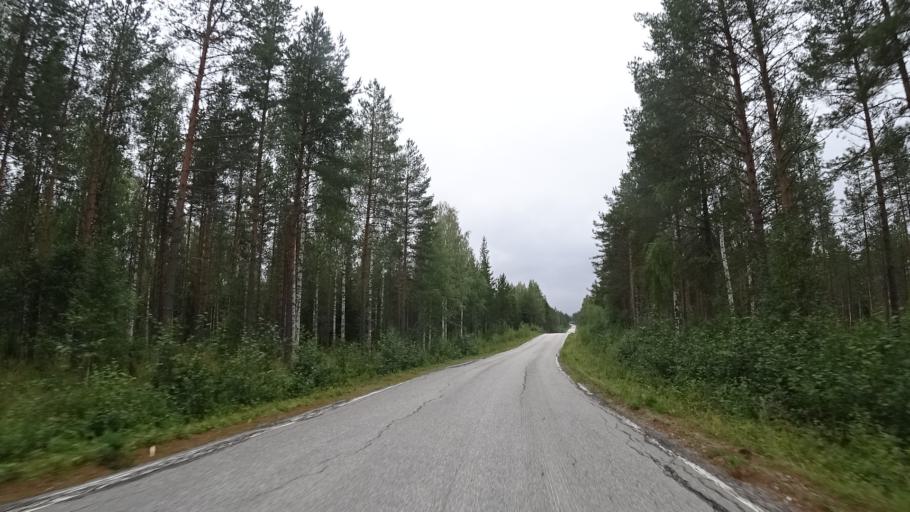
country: FI
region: North Karelia
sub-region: Pielisen Karjala
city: Lieksa
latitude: 63.3742
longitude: 30.3041
